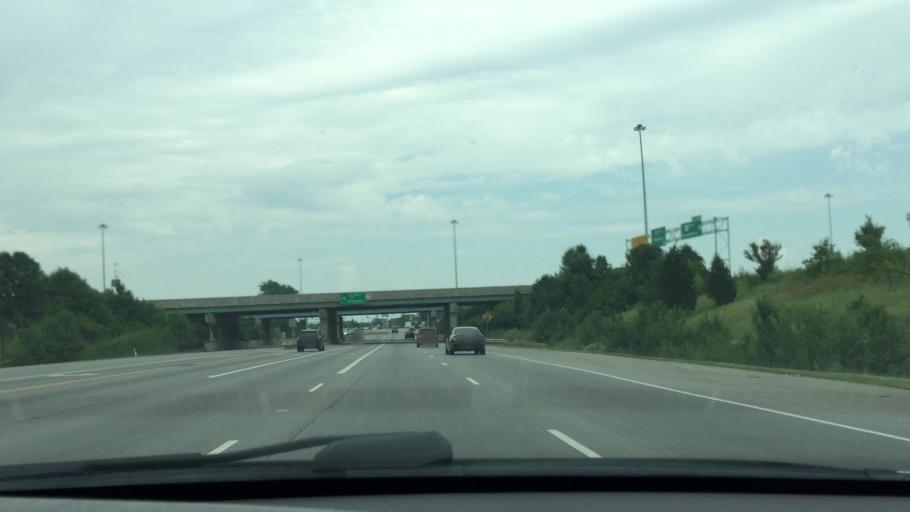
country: US
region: Ohio
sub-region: Franklin County
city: Reynoldsburg
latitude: 39.9324
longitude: -82.7890
